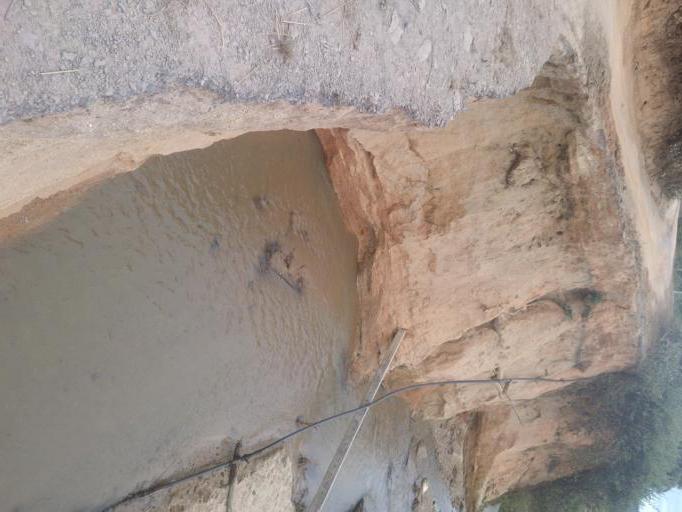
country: LA
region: Xiangkhoang
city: Muang Phonsavan
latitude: 19.3416
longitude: 103.5527
